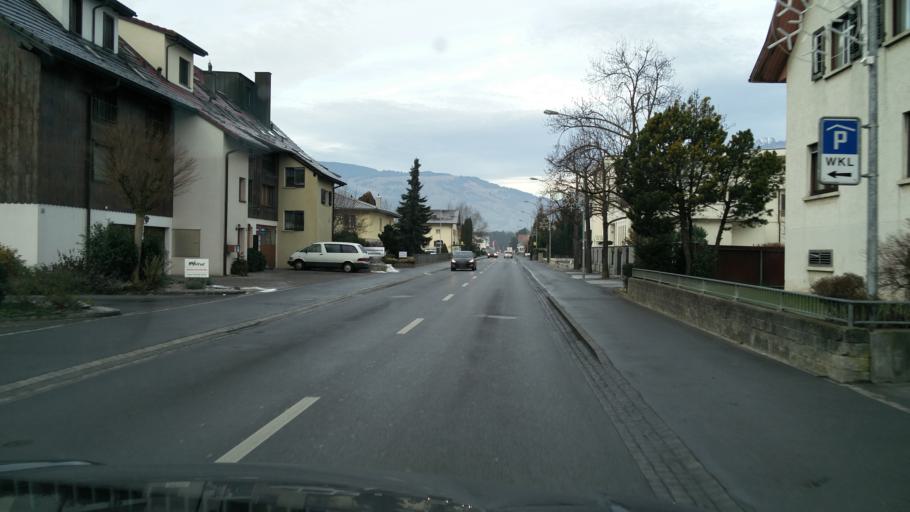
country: LI
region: Schaan
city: Schaan
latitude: 47.1683
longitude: 9.5031
